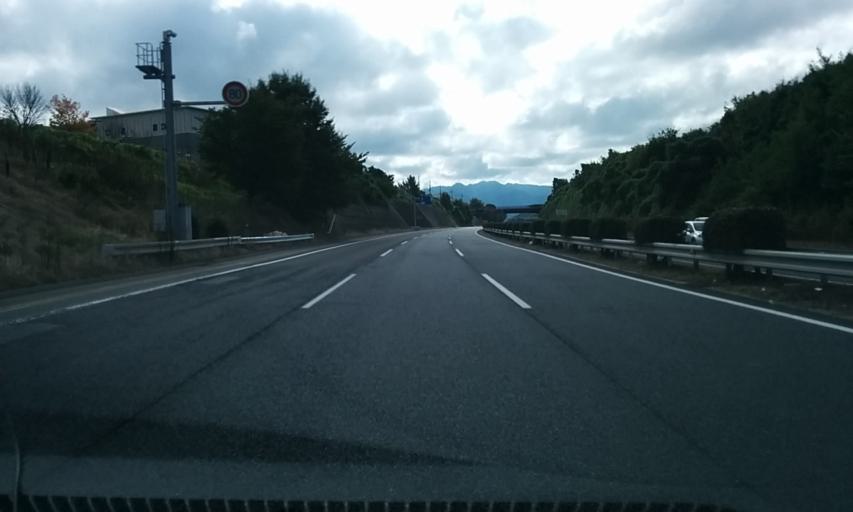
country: JP
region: Hyogo
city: Sandacho
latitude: 34.8629
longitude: 135.2135
